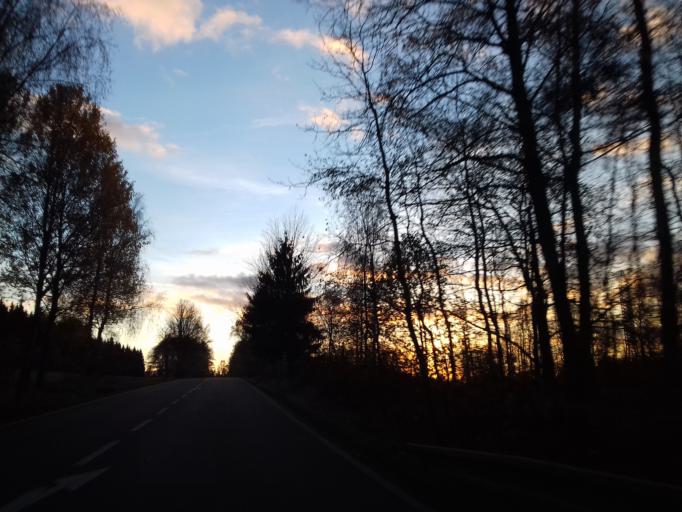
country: CZ
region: Pardubicky
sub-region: Okres Chrudim
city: Hlinsko
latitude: 49.7408
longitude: 15.8827
